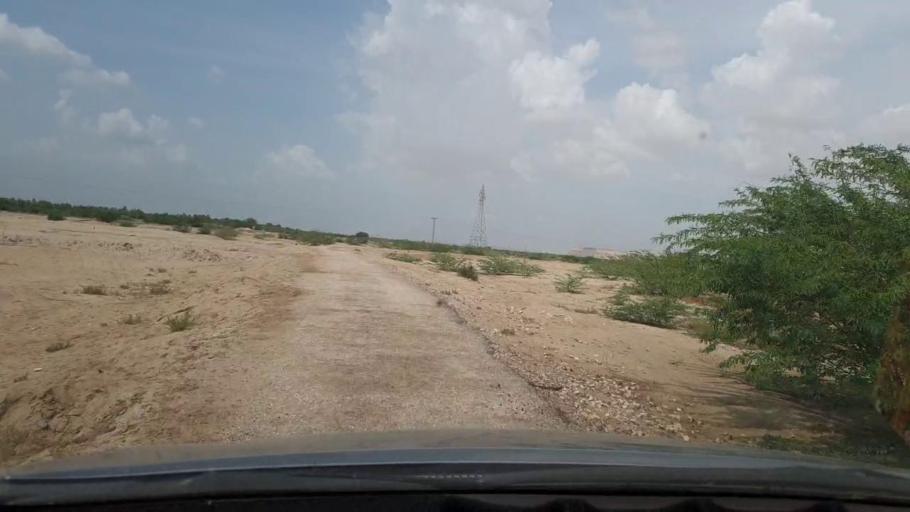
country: PK
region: Sindh
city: Khairpur
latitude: 27.4753
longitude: 68.8607
